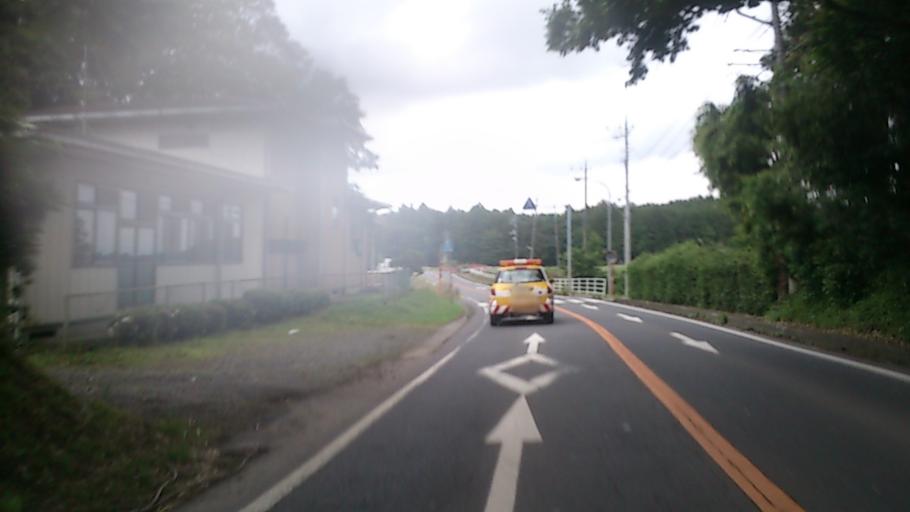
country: JP
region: Ibaraki
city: Okunoya
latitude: 36.2608
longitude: 140.3307
